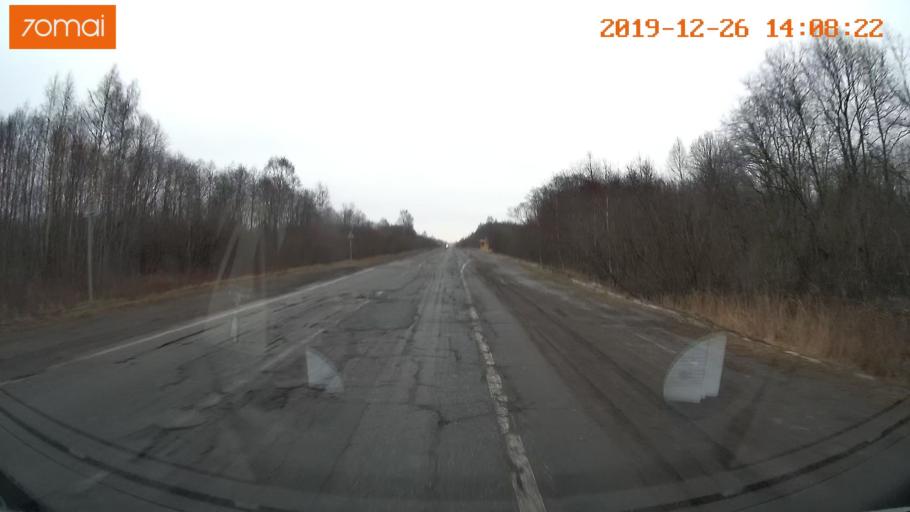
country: RU
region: Jaroslavl
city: Poshekhon'ye
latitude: 58.5087
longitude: 38.9107
